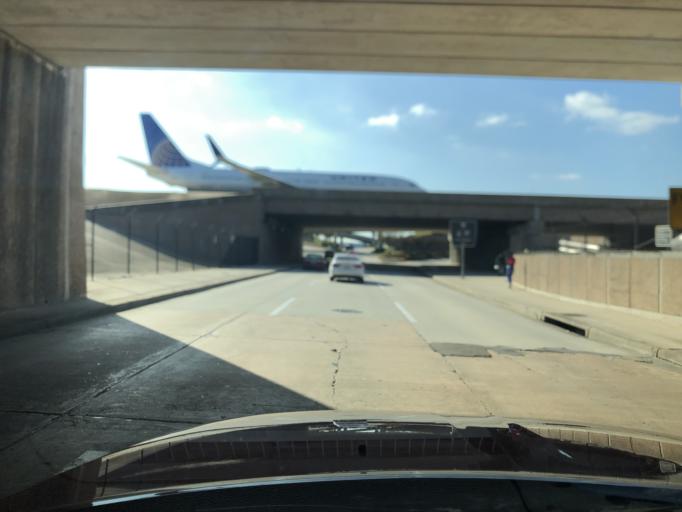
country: US
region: Texas
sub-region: Harris County
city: Aldine
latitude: 29.9839
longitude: -95.3428
